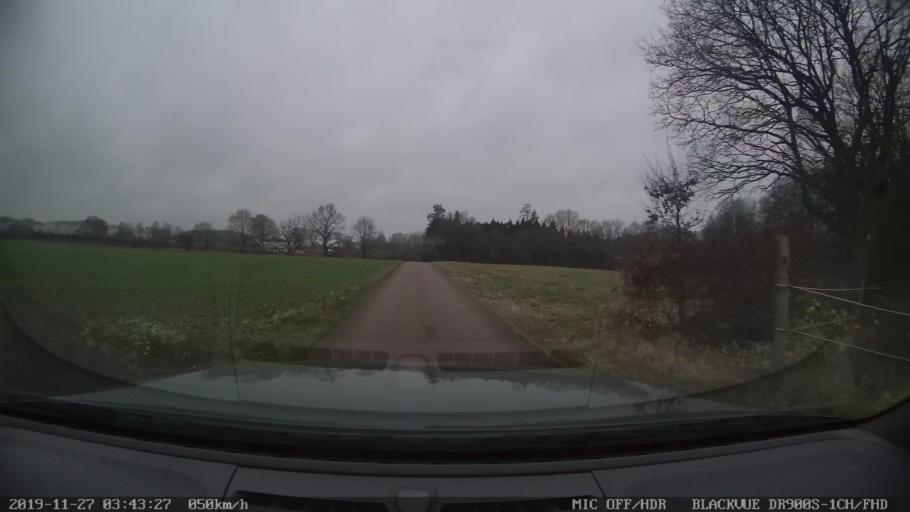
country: SE
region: Skane
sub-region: Hoganas Kommun
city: Hoganas
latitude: 56.2652
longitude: 12.5513
